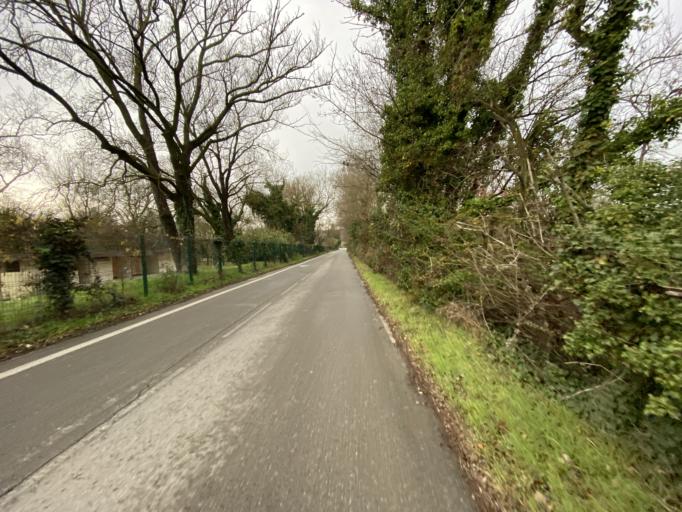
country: FR
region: Provence-Alpes-Cote d'Azur
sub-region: Departement du Vaucluse
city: Avignon
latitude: 43.9563
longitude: 4.8056
